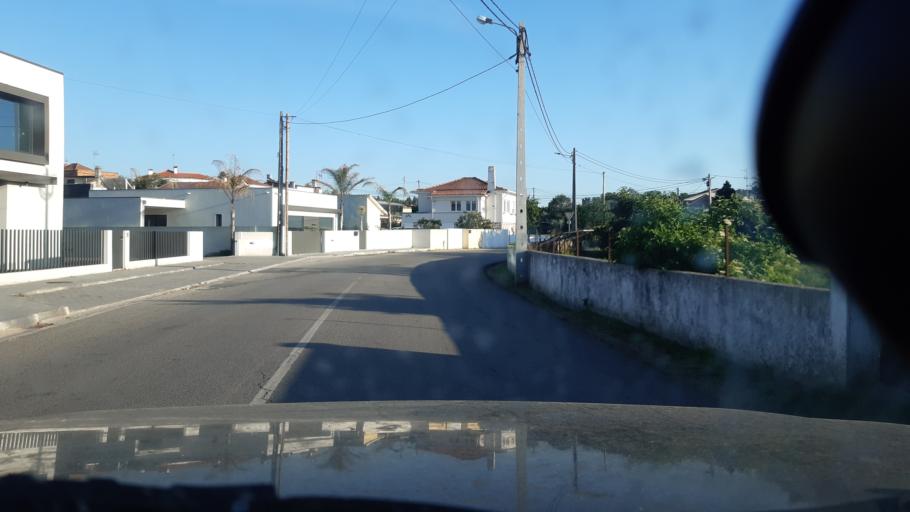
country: PT
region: Aveiro
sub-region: Agueda
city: Valongo
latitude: 40.6140
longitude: -8.4348
